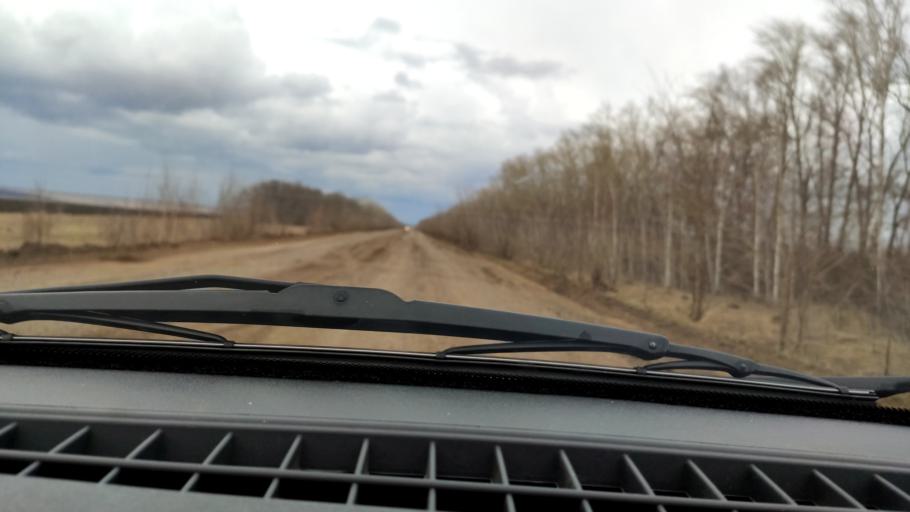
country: RU
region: Bashkortostan
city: Semiletka
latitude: 55.2668
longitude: 54.6361
